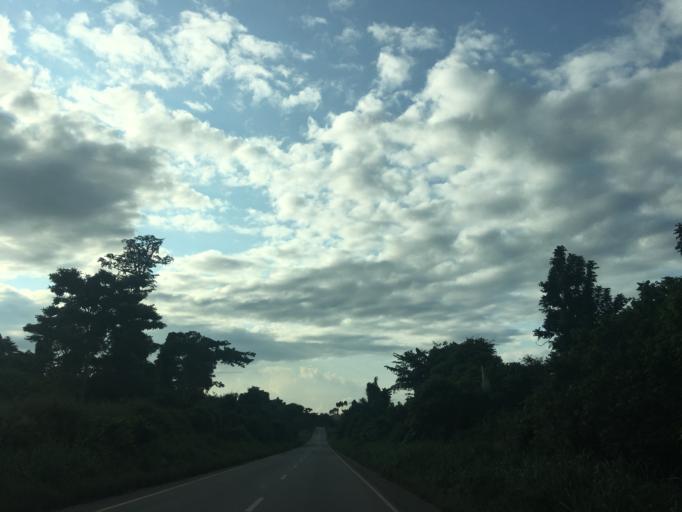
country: GH
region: Western
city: Bibiani
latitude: 6.3434
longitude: -2.2746
